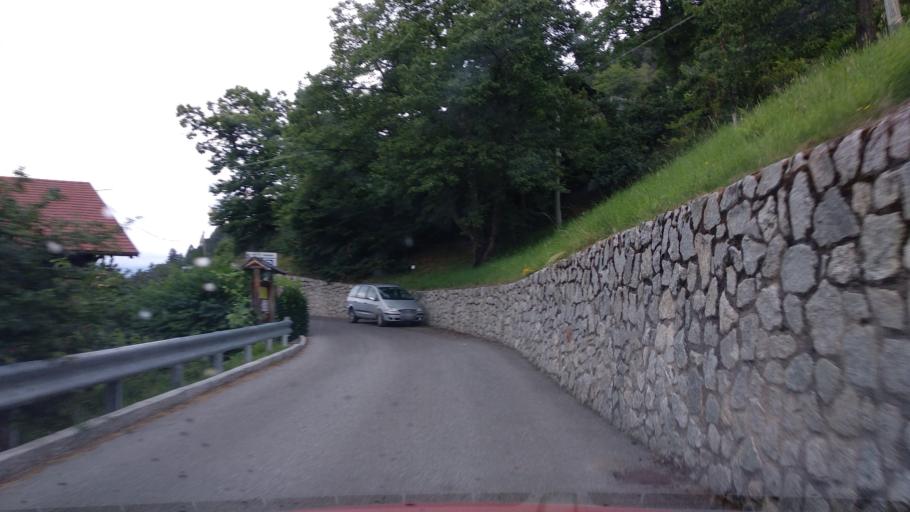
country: IT
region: Trentino-Alto Adige
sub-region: Bolzano
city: Scena
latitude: 46.7017
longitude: 11.2035
